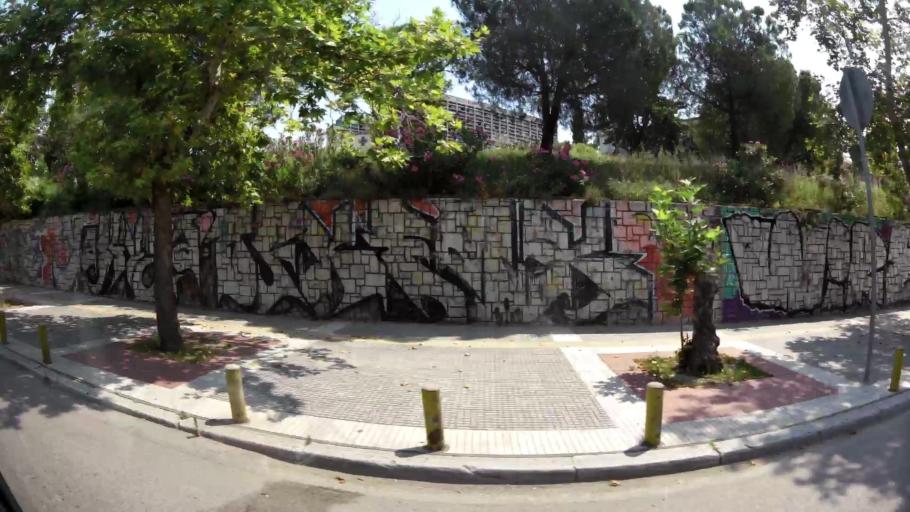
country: GR
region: Central Macedonia
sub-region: Nomos Thessalonikis
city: Agios Pavlos
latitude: 40.6304
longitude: 22.9618
